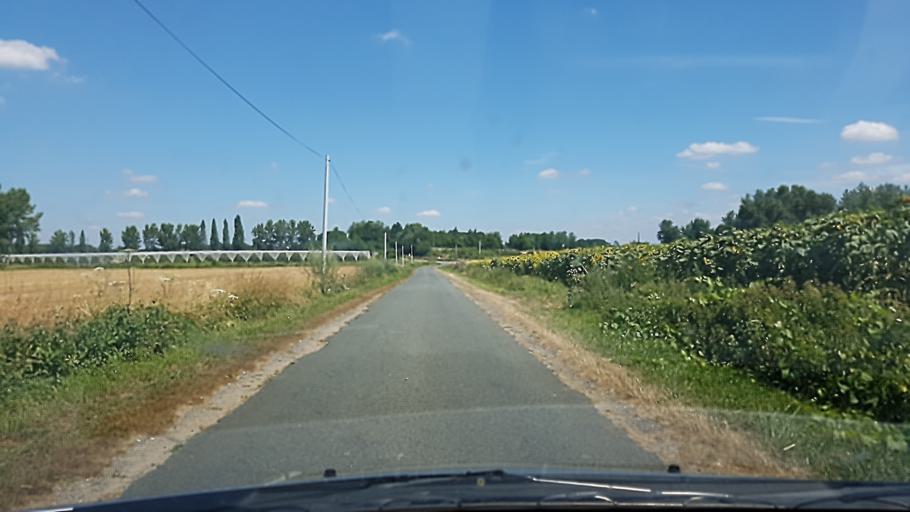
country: FR
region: Pays de la Loire
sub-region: Departement de Maine-et-Loire
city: Le Plessis-Grammoire
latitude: 47.5135
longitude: -0.4086
